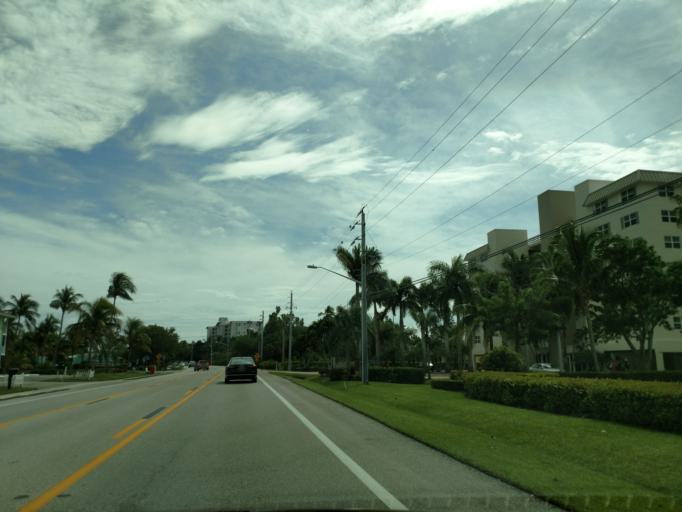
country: US
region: Florida
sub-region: Lee County
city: Fort Myers Beach
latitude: 26.4079
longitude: -81.8969
